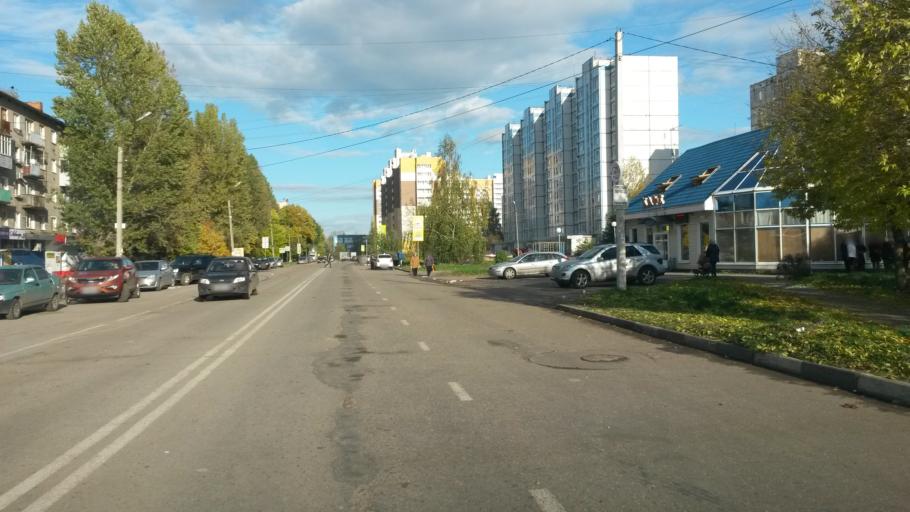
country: RU
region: Jaroslavl
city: Yaroslavl
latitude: 57.5682
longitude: 39.9273
